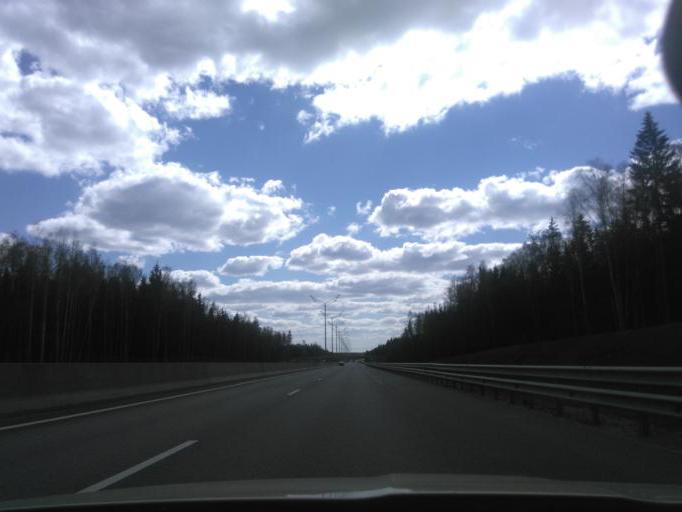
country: RU
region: Moskovskaya
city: Mendeleyevo
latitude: 56.0675
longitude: 37.2269
